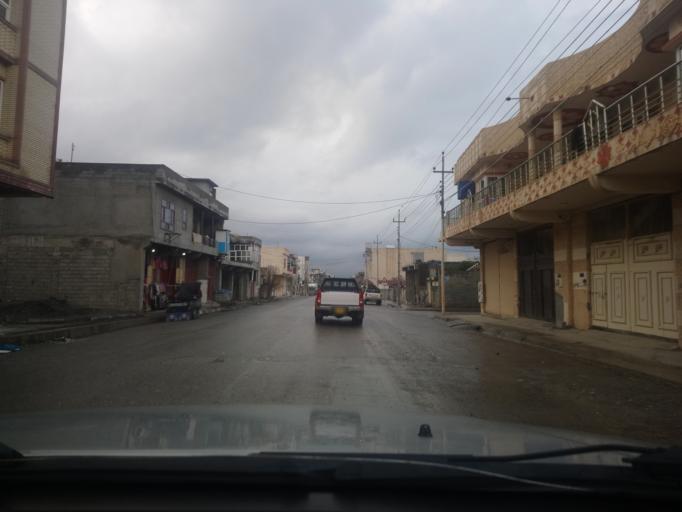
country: IQ
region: As Sulaymaniyah
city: Qeladize
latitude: 36.1833
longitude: 45.1340
